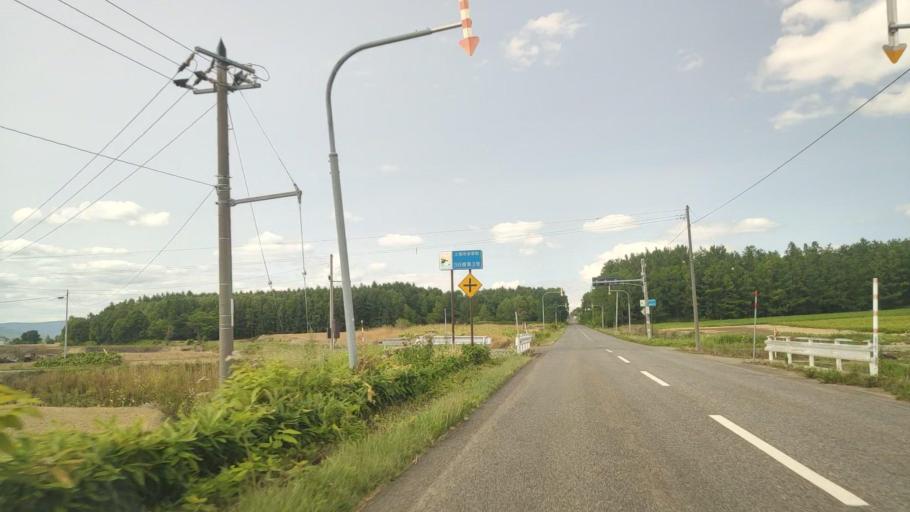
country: JP
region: Hokkaido
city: Nayoro
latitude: 44.2406
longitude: 142.4157
